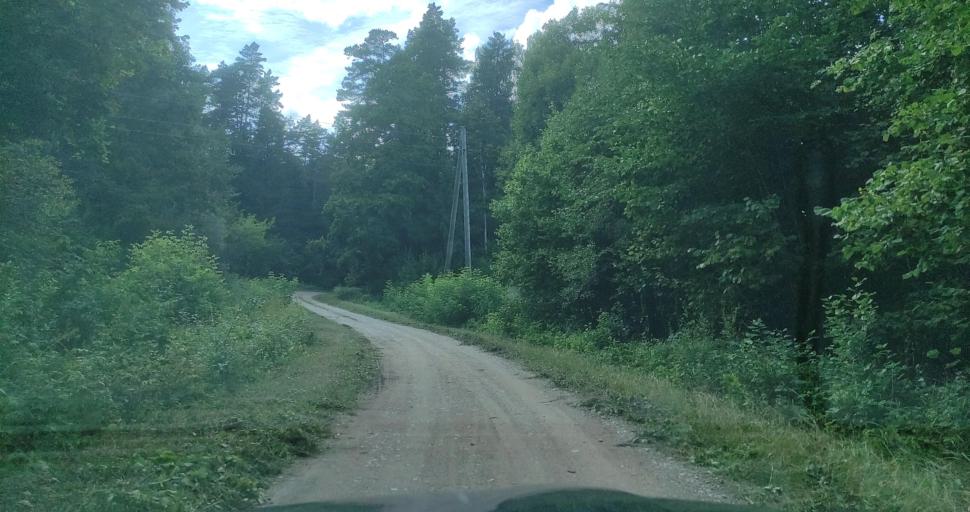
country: LV
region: Kuldigas Rajons
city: Kuldiga
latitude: 56.9907
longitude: 22.0147
